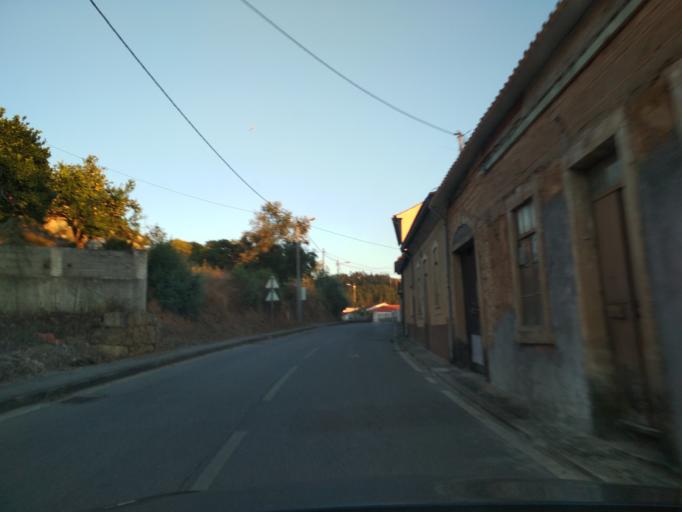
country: PT
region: Coimbra
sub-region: Condeixa-A-Nova
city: Condeixa-a-Nova
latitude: 40.1709
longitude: -8.4802
